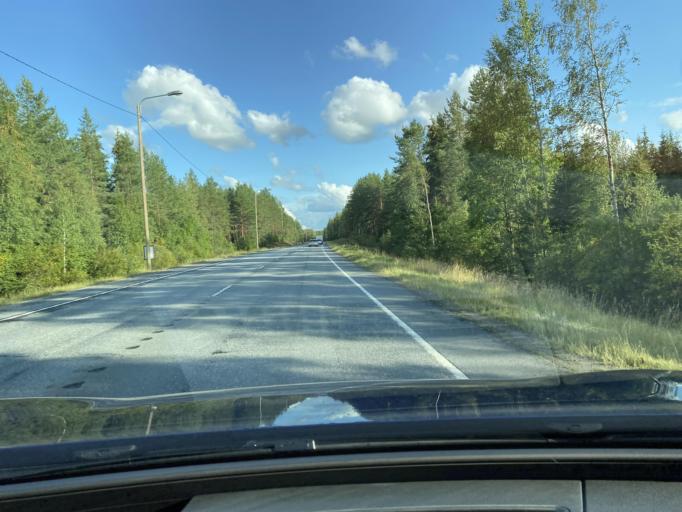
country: FI
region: Southern Ostrobothnia
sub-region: Seinaejoki
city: Alahaermae
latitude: 63.1227
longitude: 22.9237
